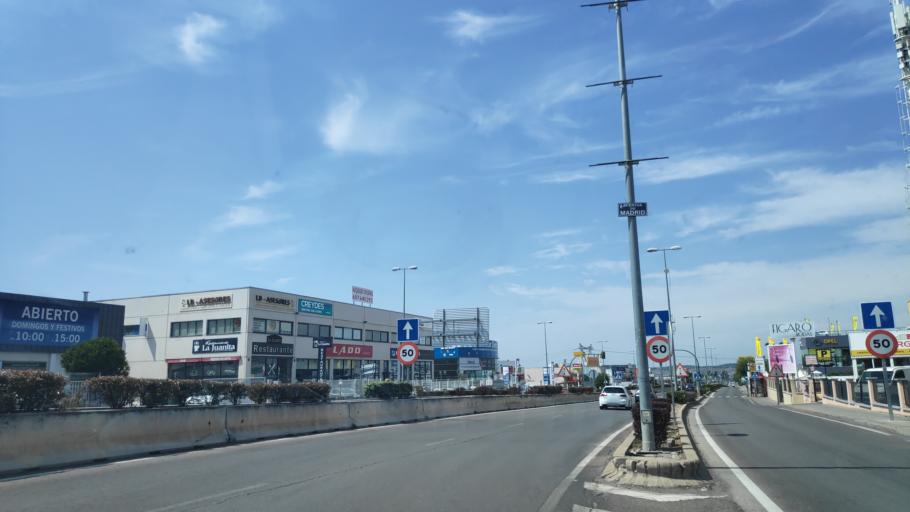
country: ES
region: Madrid
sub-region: Provincia de Madrid
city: Arganda
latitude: 40.3046
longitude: -3.4543
